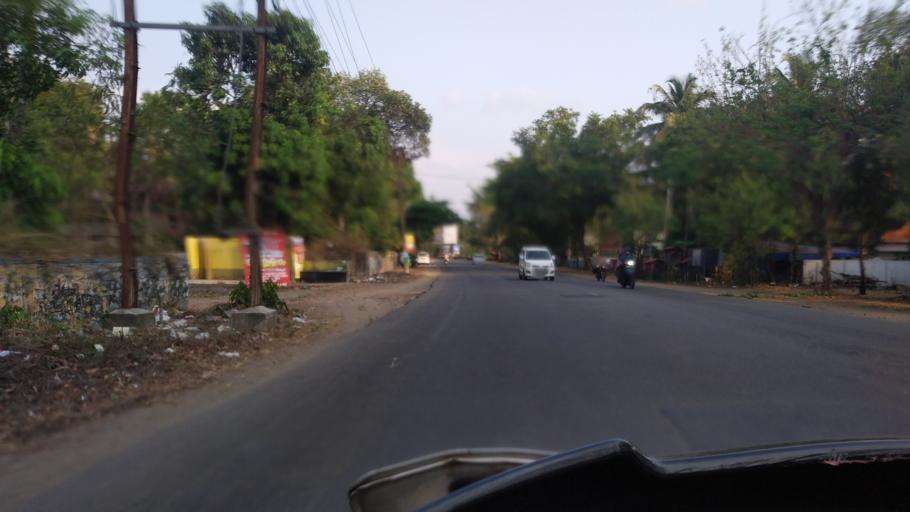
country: IN
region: Kerala
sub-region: Thrissur District
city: Thanniyam
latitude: 10.4384
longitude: 76.0960
